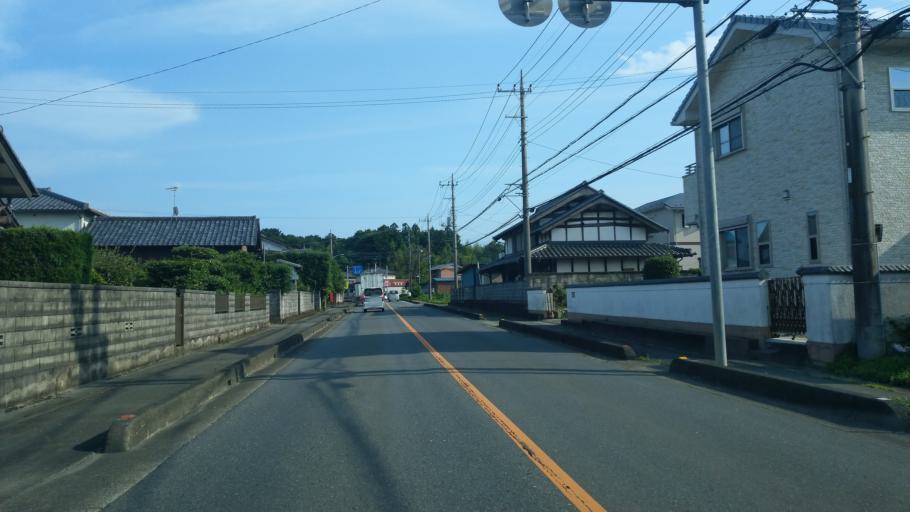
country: JP
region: Saitama
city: Ogawa
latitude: 36.0903
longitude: 139.2801
